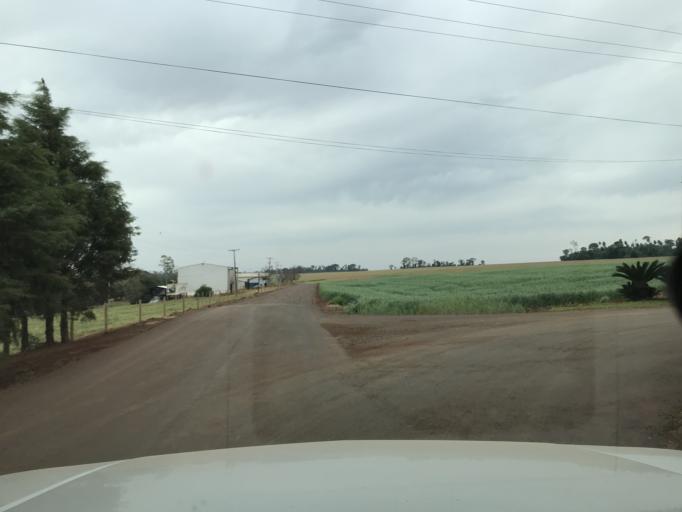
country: BR
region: Parana
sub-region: Marechal Candido Rondon
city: Marechal Candido Rondon
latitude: -24.4604
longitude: -53.9670
